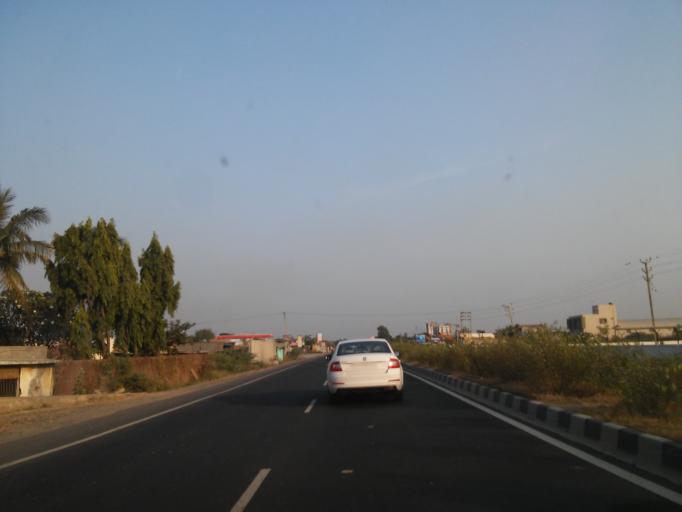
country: IN
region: Gujarat
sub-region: Ahmadabad
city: Sanand
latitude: 23.0254
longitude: 72.3139
